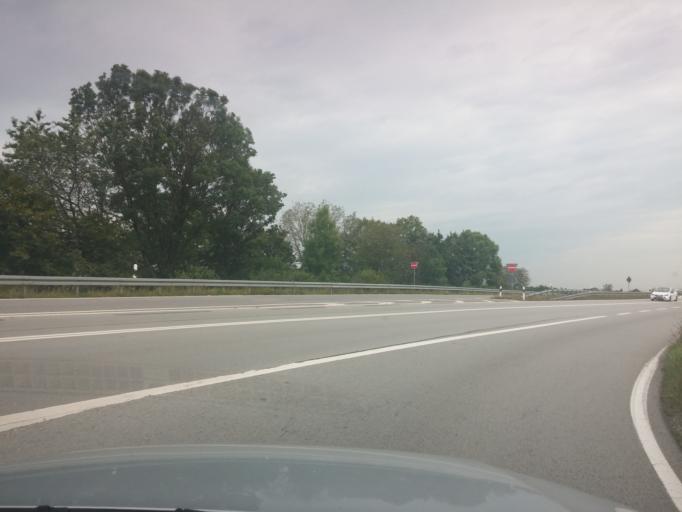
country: DE
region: Bavaria
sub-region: Upper Bavaria
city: Aschheim
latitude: 48.1671
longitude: 11.7345
